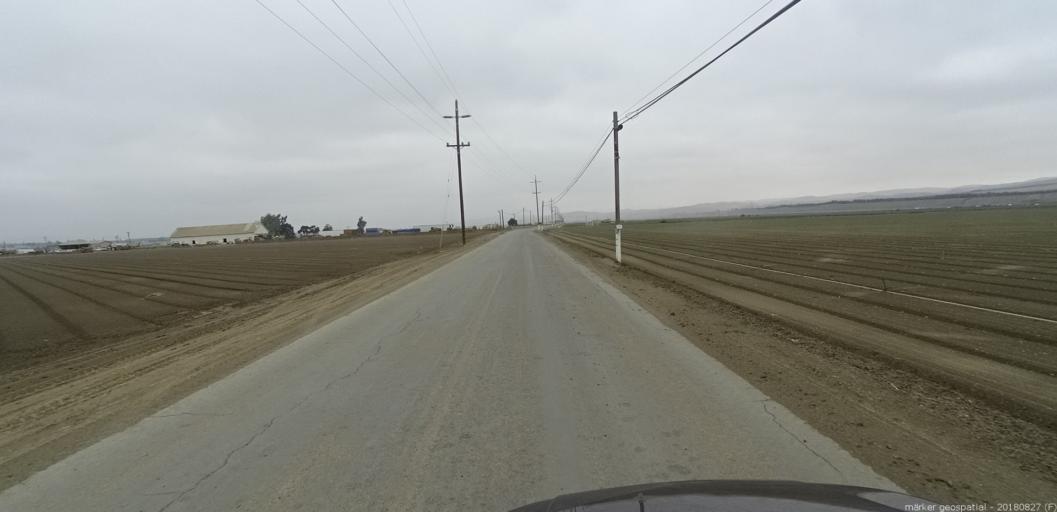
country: US
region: California
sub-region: Monterey County
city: King City
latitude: 36.2445
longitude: -121.1472
